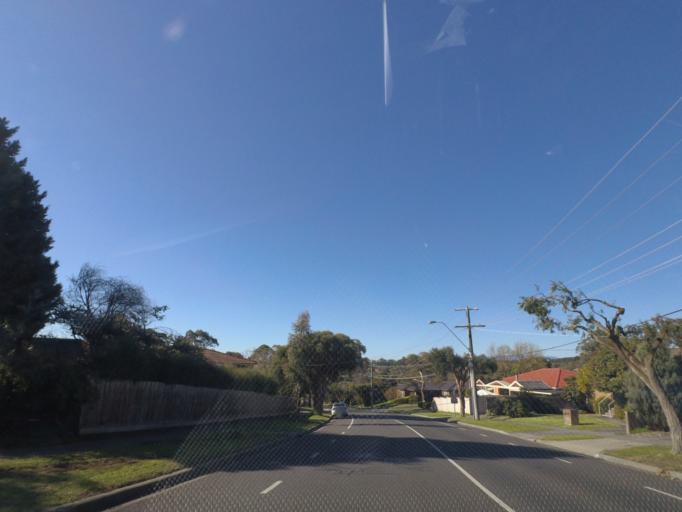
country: AU
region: Victoria
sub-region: Maroondah
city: Croydon Hills
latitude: -37.7775
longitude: 145.2570
